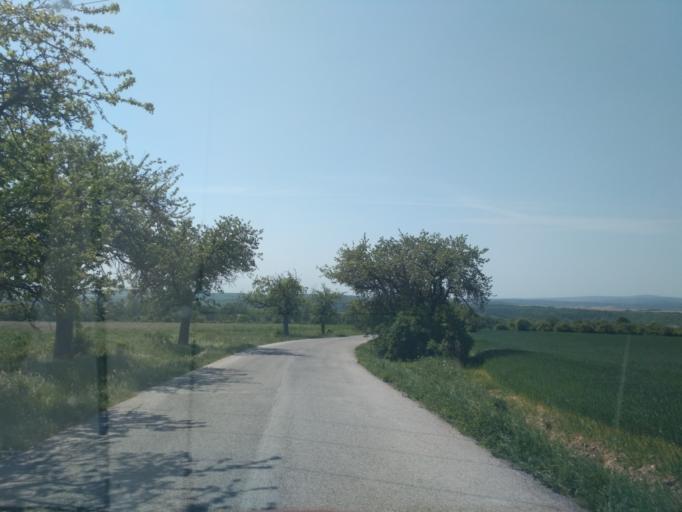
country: SK
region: Kosicky
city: Kosice
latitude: 48.8217
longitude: 21.4463
